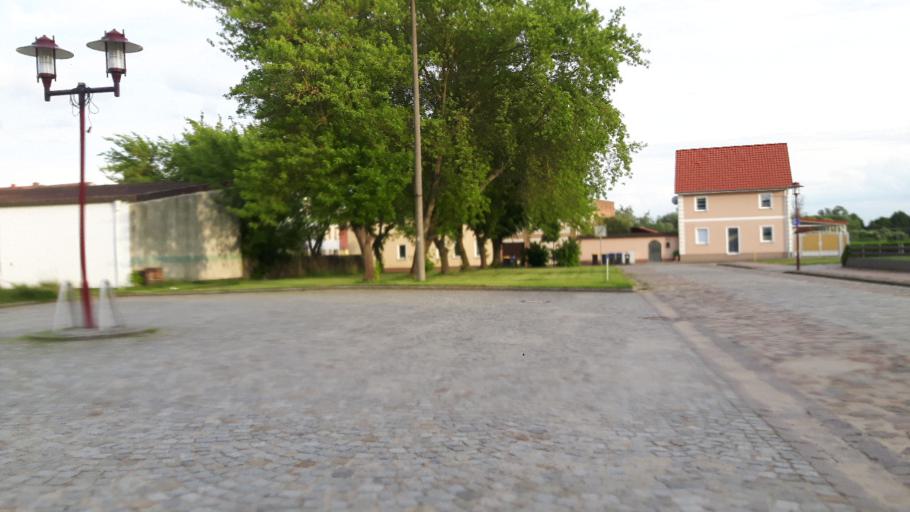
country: DE
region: Brandenburg
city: Gartz
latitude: 53.2076
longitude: 14.3922
